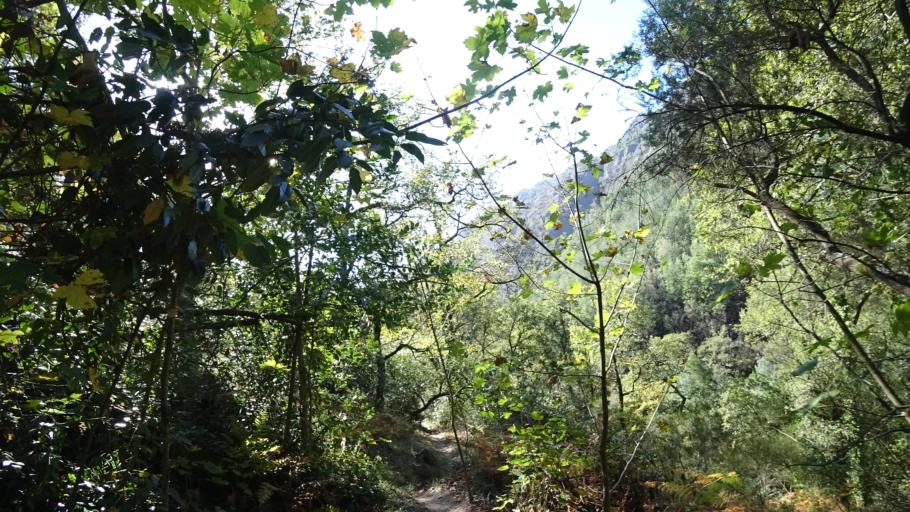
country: PT
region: Braga
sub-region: Vieira do Minho
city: Real
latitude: 41.7531
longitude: -8.1509
